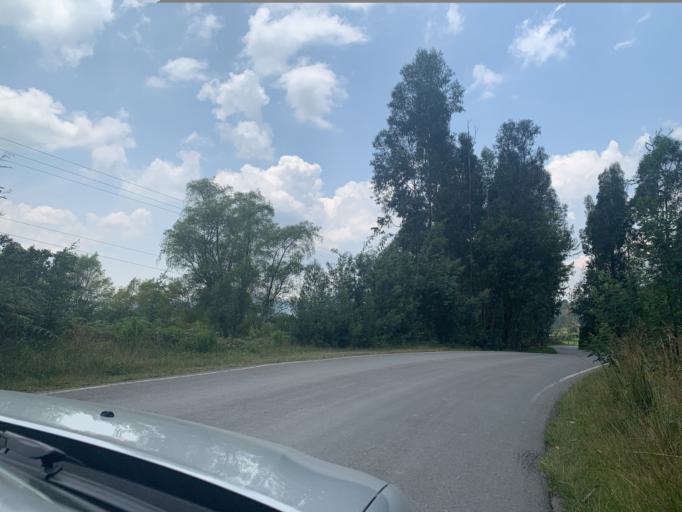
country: CO
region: Boyaca
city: Chiquinquira
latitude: 5.5405
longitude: -73.7499
